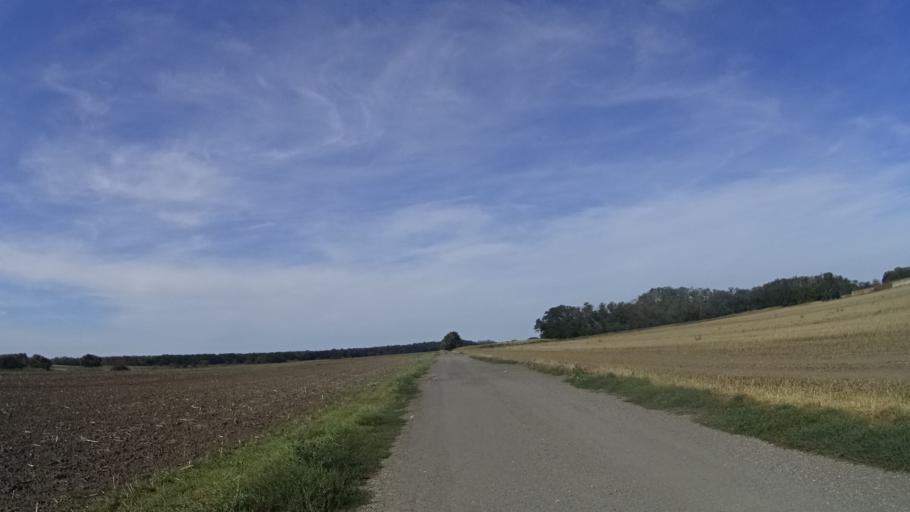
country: AT
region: Lower Austria
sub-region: Politischer Bezirk Ganserndorf
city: Durnkrut
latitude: 48.4454
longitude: 16.8802
